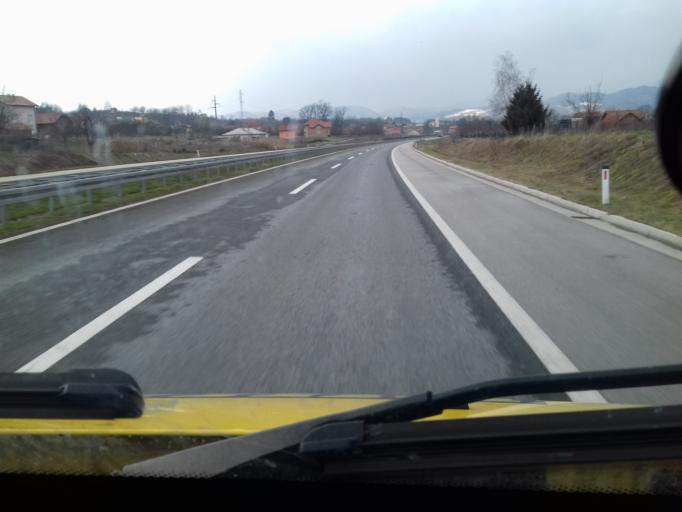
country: BA
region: Federation of Bosnia and Herzegovina
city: Gornje Mostre
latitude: 44.0074
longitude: 18.1481
